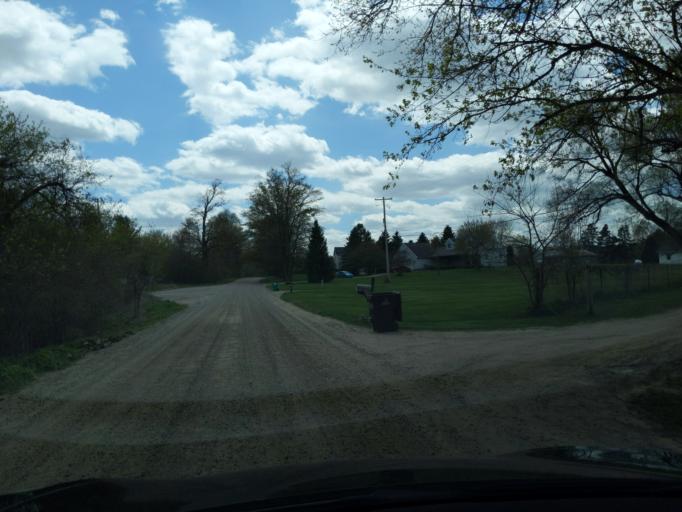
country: US
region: Michigan
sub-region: Eaton County
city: Dimondale
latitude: 42.6349
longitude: -84.6142
